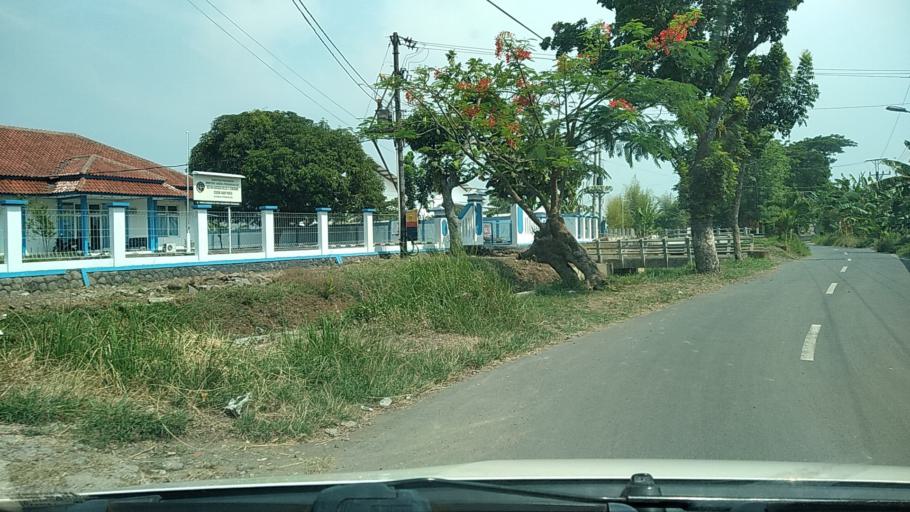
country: ID
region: Central Java
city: Semarang
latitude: -6.9767
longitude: 110.3436
